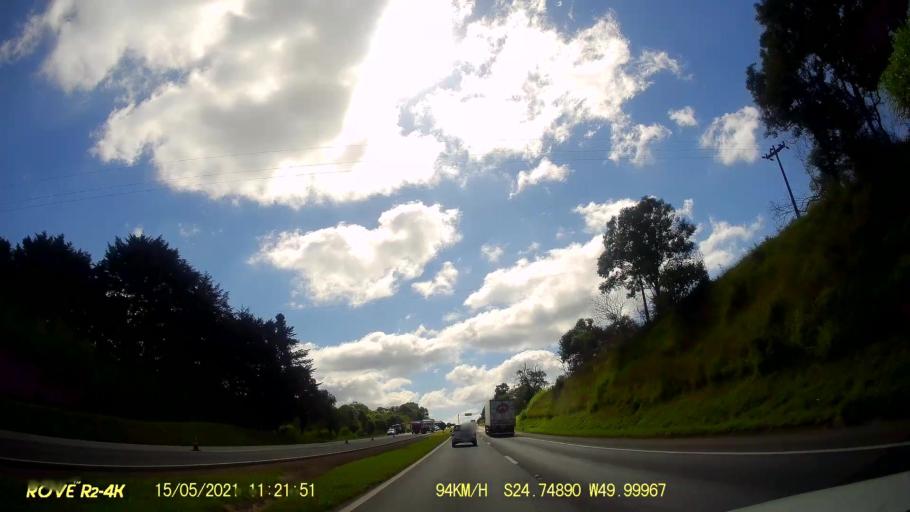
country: BR
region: Parana
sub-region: Castro
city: Castro
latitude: -24.7489
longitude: -49.9995
